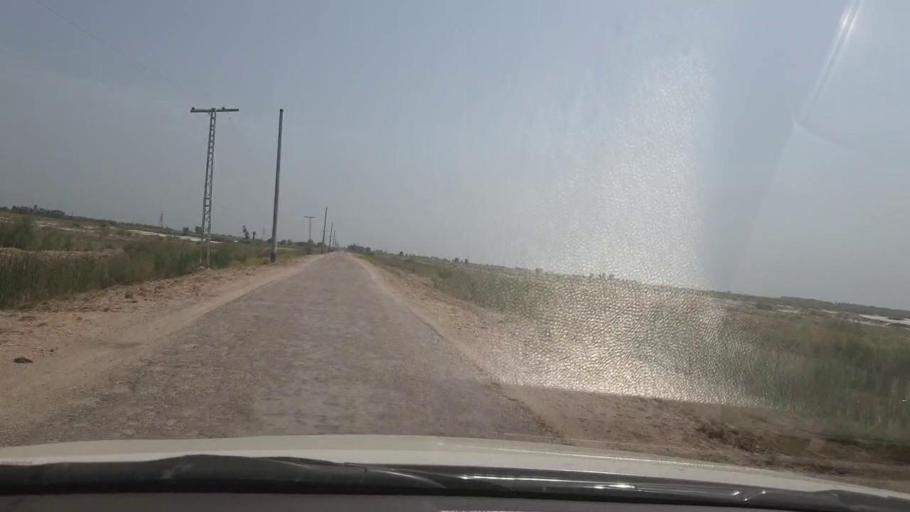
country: PK
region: Sindh
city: Garhi Yasin
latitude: 27.9527
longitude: 68.5058
